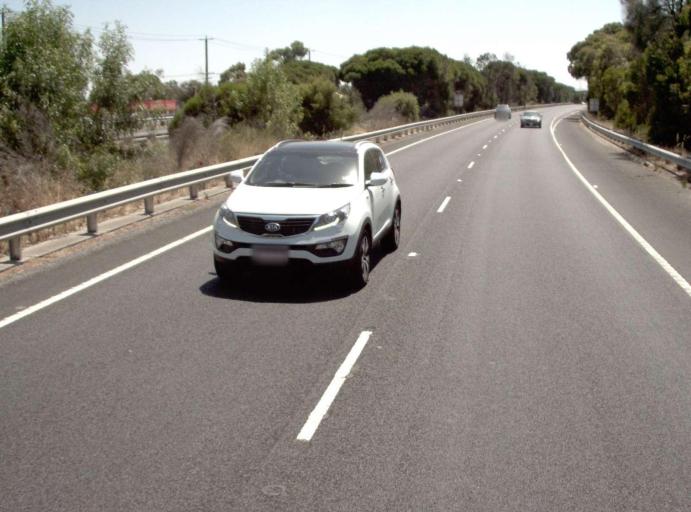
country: AU
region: Victoria
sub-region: Frankston
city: Frankston North
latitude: -38.1141
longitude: 145.1377
